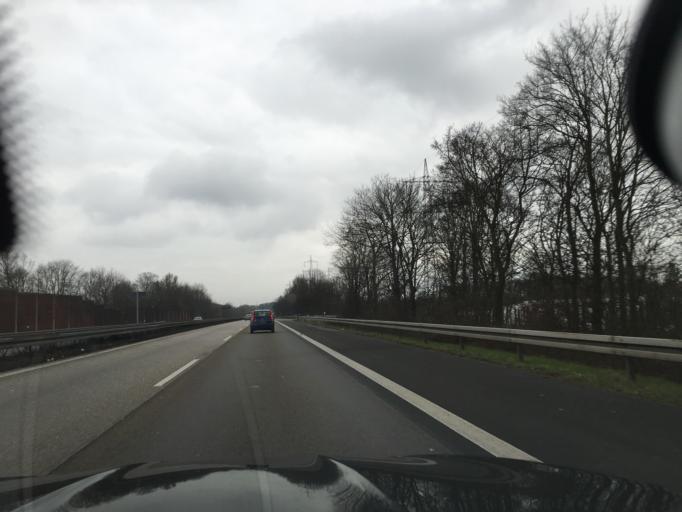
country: DE
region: North Rhine-Westphalia
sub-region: Regierungsbezirk Koln
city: Wahn-Heide
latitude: 50.8580
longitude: 7.0968
